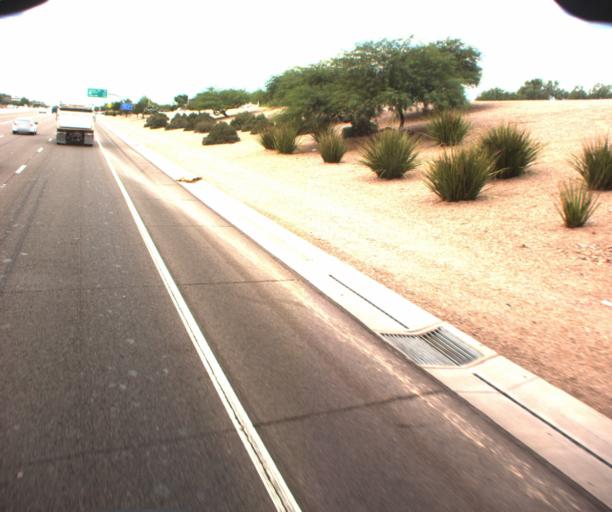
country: US
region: Arizona
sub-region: Maricopa County
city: Chandler
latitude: 33.2874
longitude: -111.8591
